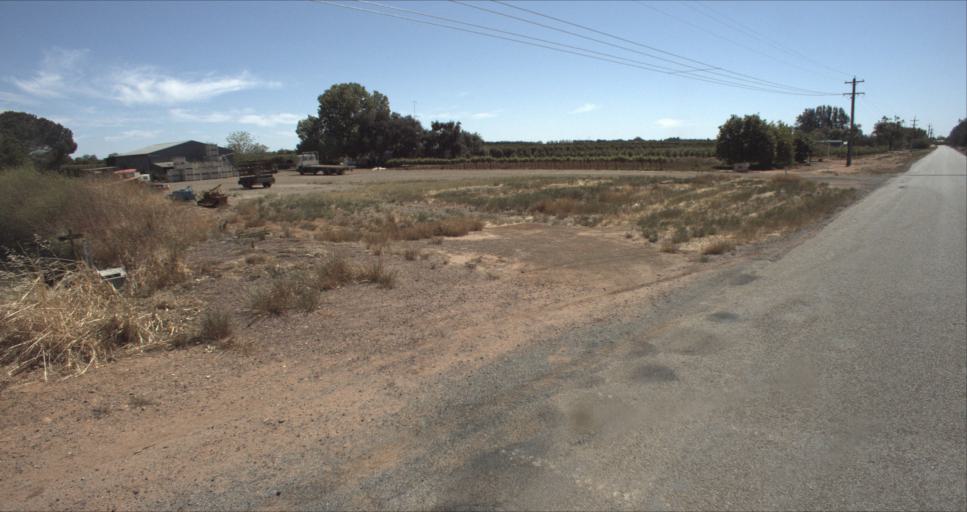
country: AU
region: New South Wales
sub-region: Leeton
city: Leeton
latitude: -34.5386
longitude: 146.3605
